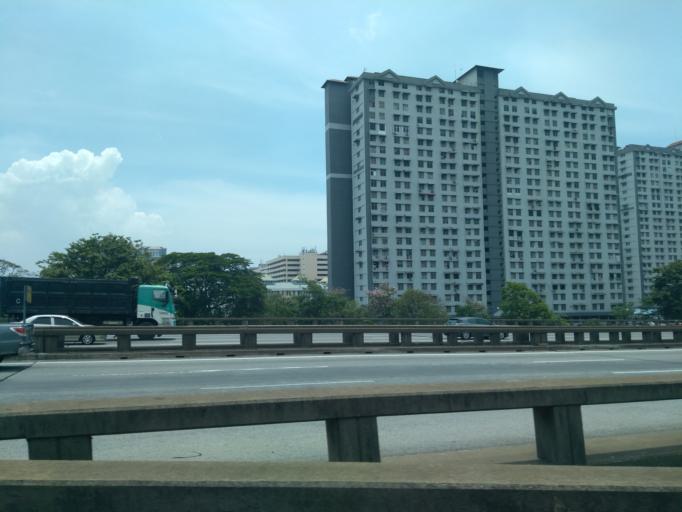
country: MY
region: Penang
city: Perai
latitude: 5.3739
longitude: 100.4018
